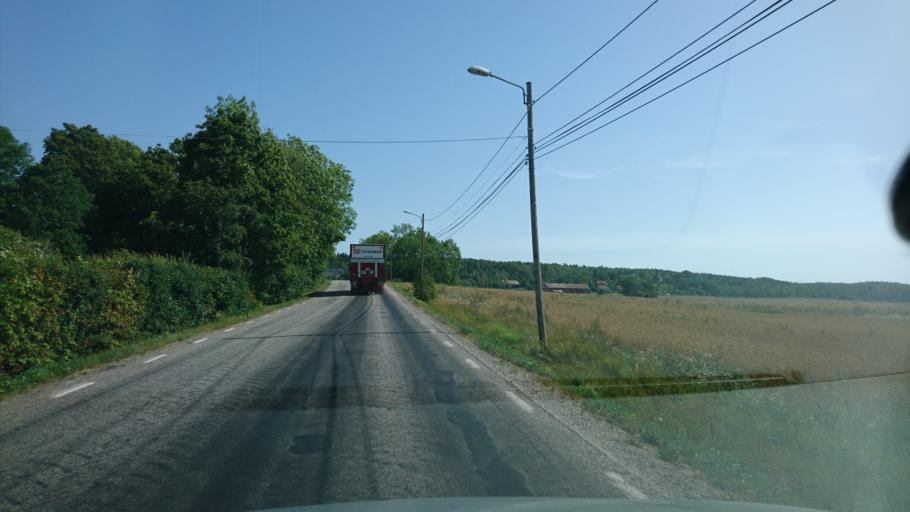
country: SE
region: Soedermanland
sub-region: Strangnas Kommun
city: Strangnas
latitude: 59.3513
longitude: 17.0566
